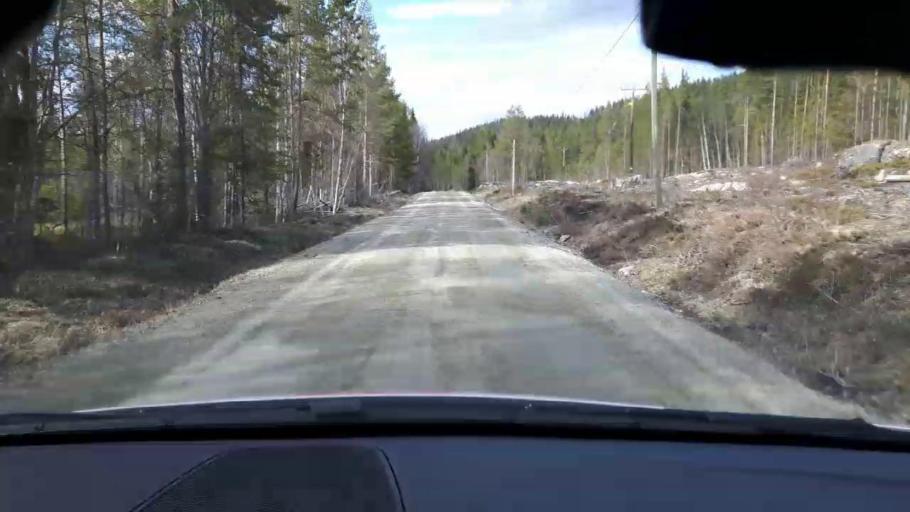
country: SE
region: Jaemtland
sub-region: Bergs Kommun
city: Hoverberg
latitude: 62.6765
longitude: 14.7468
